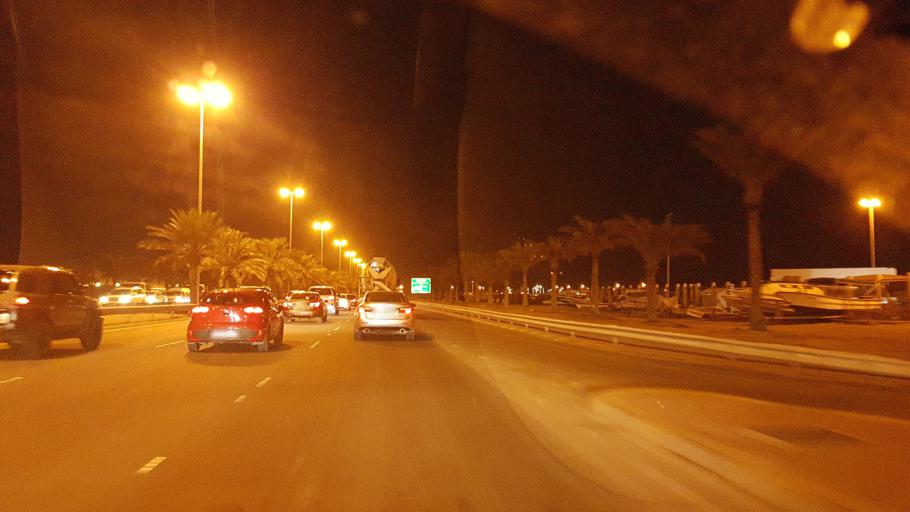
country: BH
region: Muharraq
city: Al Hadd
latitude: 26.2452
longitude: 50.6585
